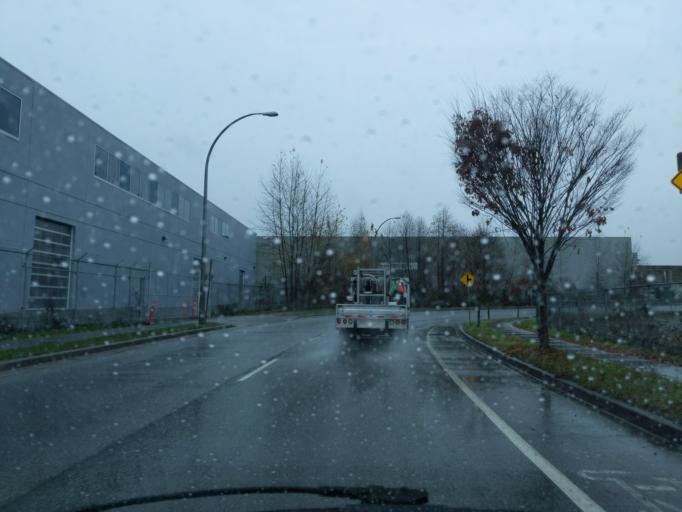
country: CA
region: British Columbia
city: Walnut Grove
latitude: 49.1819
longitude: -122.6665
